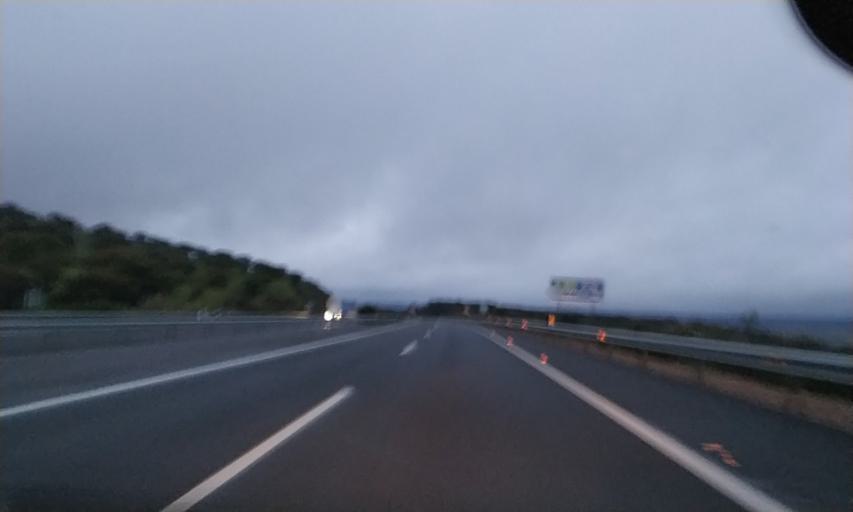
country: ES
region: Extremadura
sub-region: Provincia de Caceres
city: Alcuescar
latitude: 39.1719
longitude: -6.2705
